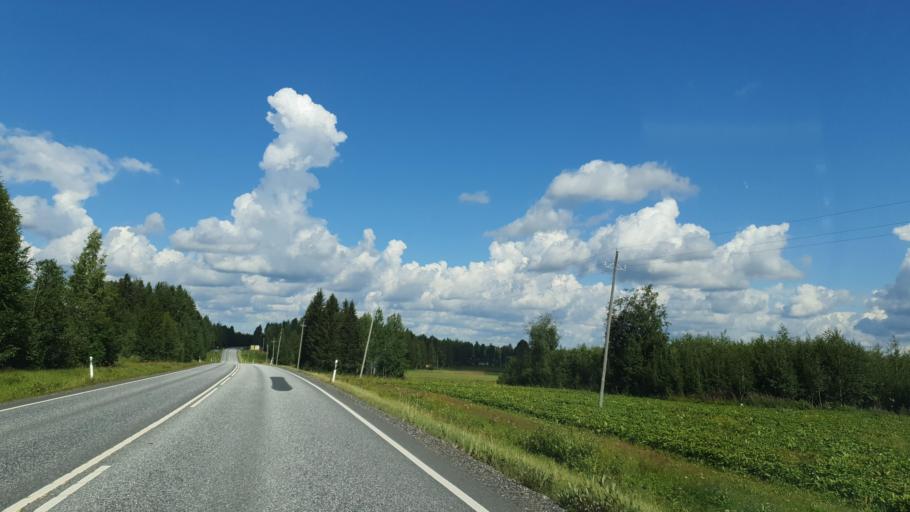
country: FI
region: Northern Savo
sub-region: Ylae-Savo
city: Sonkajaervi
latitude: 63.7989
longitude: 27.4188
